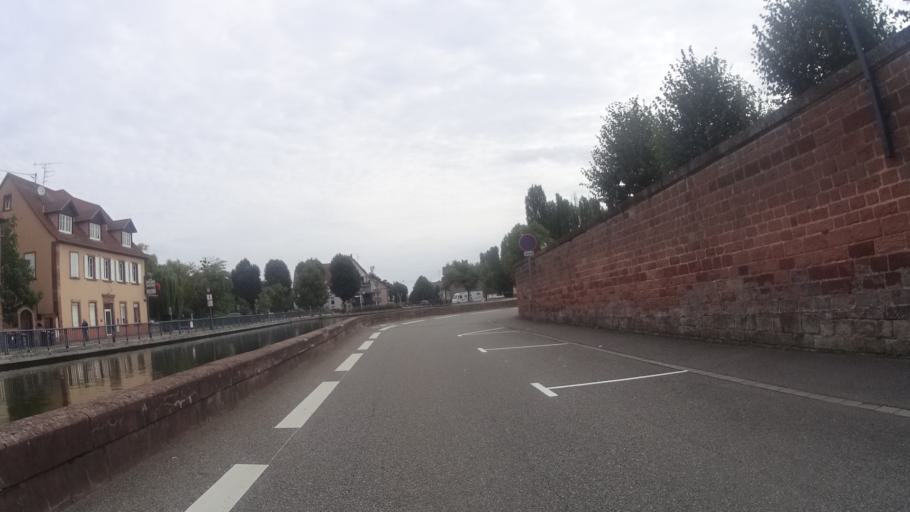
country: FR
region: Alsace
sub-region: Departement du Bas-Rhin
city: Saverne
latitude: 48.7434
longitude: 7.3641
